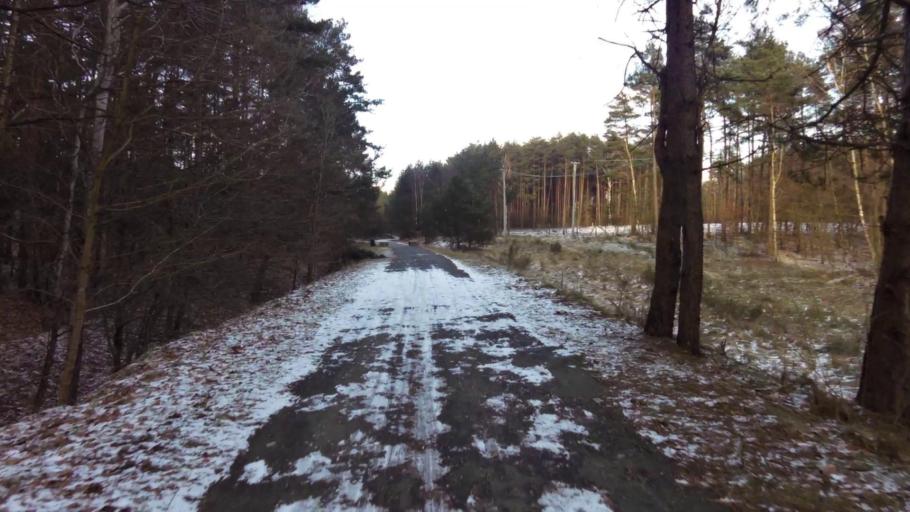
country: PL
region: West Pomeranian Voivodeship
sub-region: Powiat drawski
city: Zlocieniec
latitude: 53.5493
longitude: 16.0195
